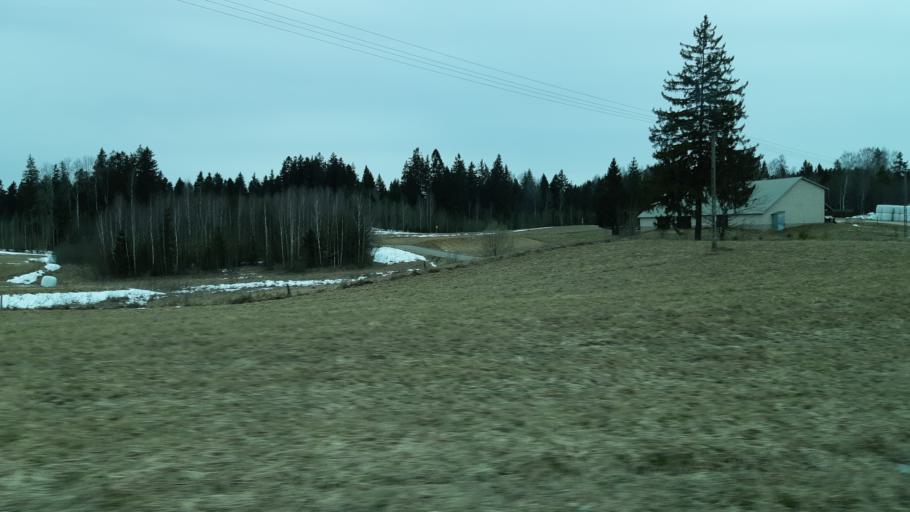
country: LT
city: Virbalis
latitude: 54.3787
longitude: 22.8197
